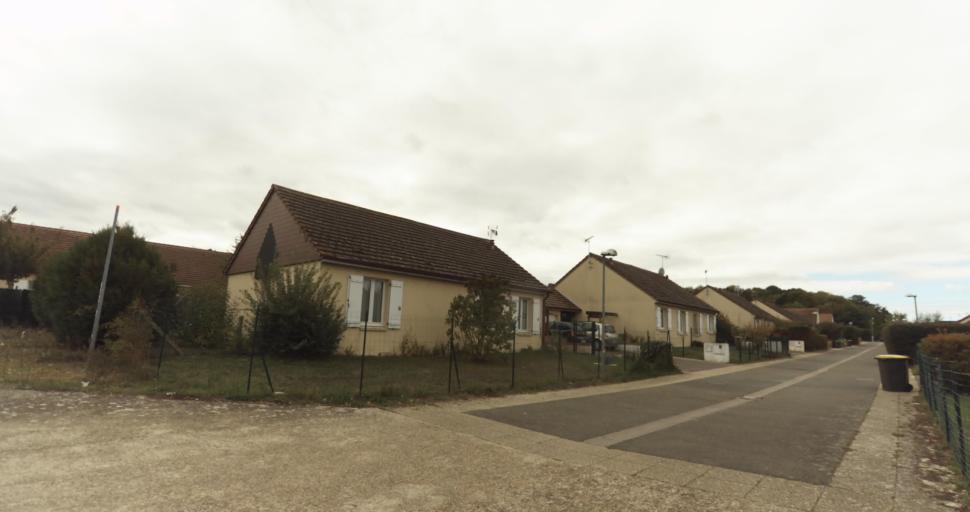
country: FR
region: Centre
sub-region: Departement d'Eure-et-Loir
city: Garnay
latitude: 48.7291
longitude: 1.3406
